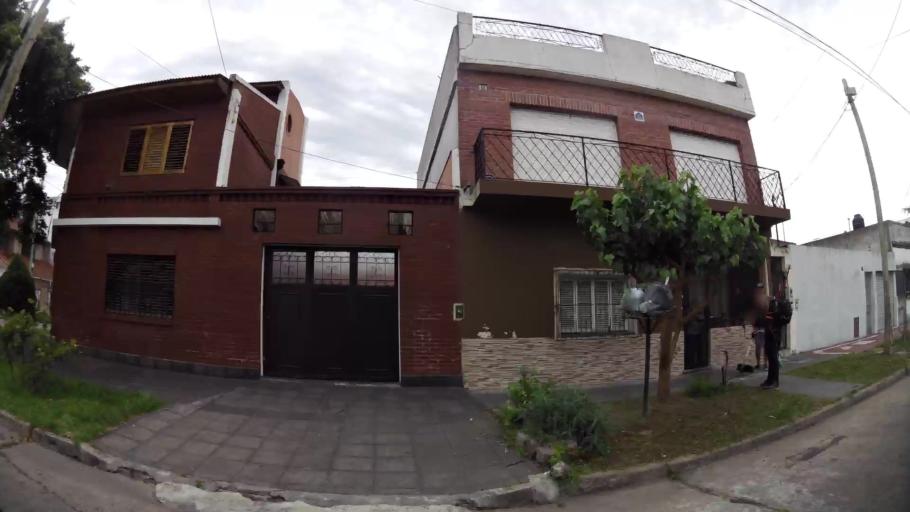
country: AR
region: Buenos Aires
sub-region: Partido de Lanus
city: Lanus
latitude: -34.6839
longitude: -58.3918
